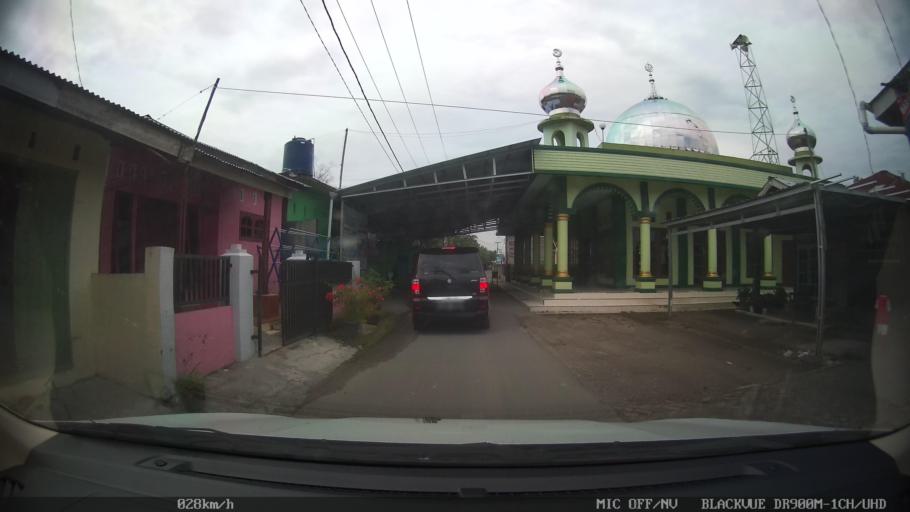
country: ID
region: North Sumatra
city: Sunggal
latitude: 3.6519
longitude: 98.5924
